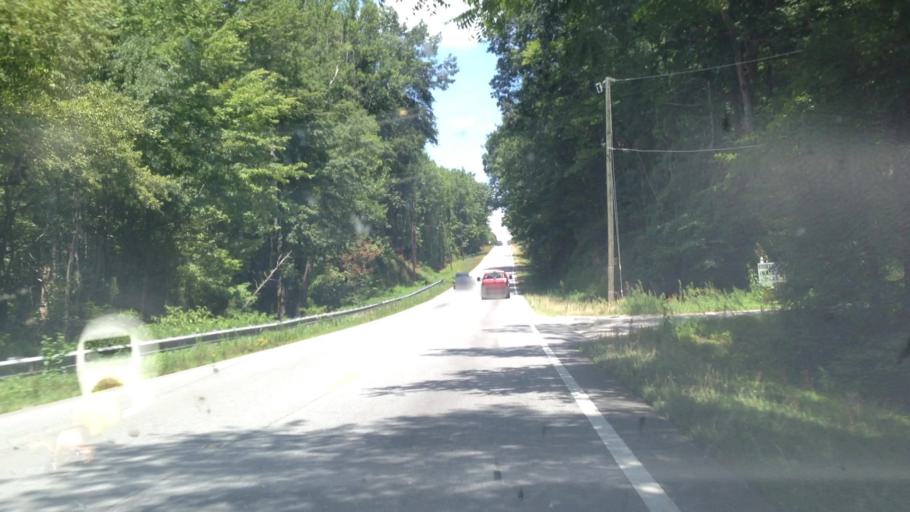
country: US
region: North Carolina
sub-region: Guilford County
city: Stokesdale
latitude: 36.2637
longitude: -79.9534
